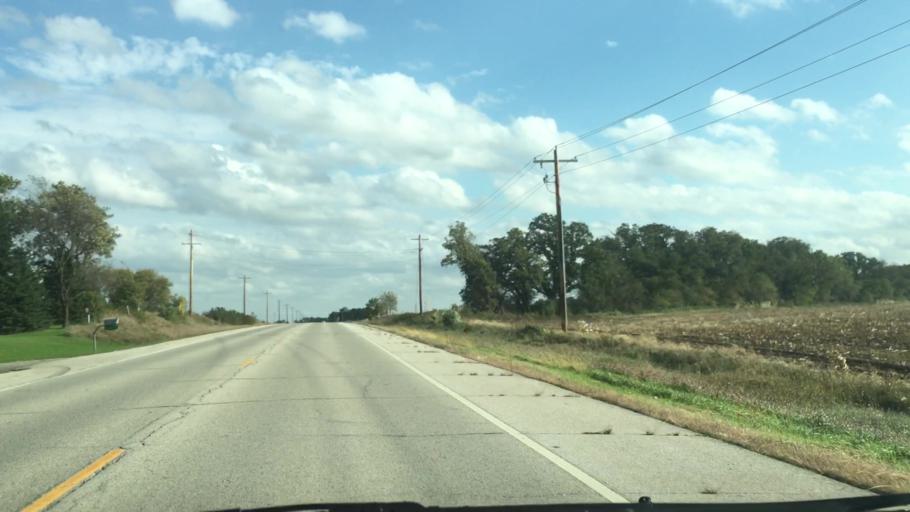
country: US
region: Minnesota
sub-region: Olmsted County
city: Eyota
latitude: 43.9253
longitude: -92.2848
